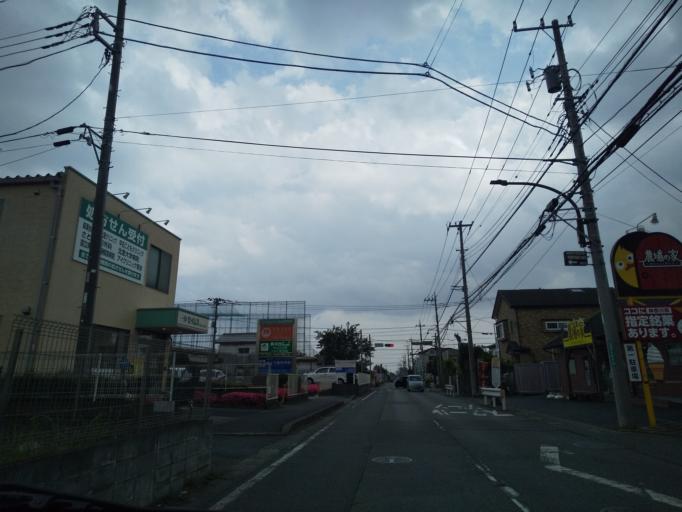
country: JP
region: Kanagawa
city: Zama
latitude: 35.5314
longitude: 139.4059
